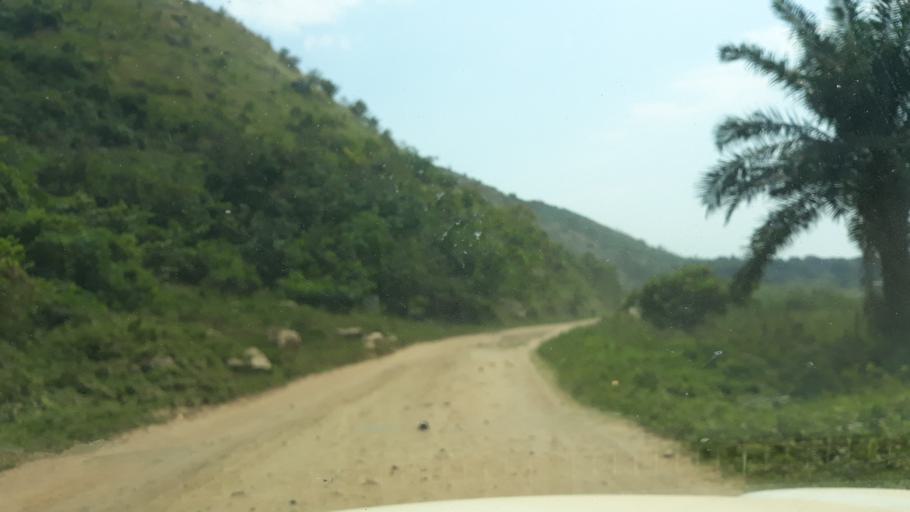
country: CD
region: South Kivu
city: Uvira
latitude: -3.5751
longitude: 29.1459
